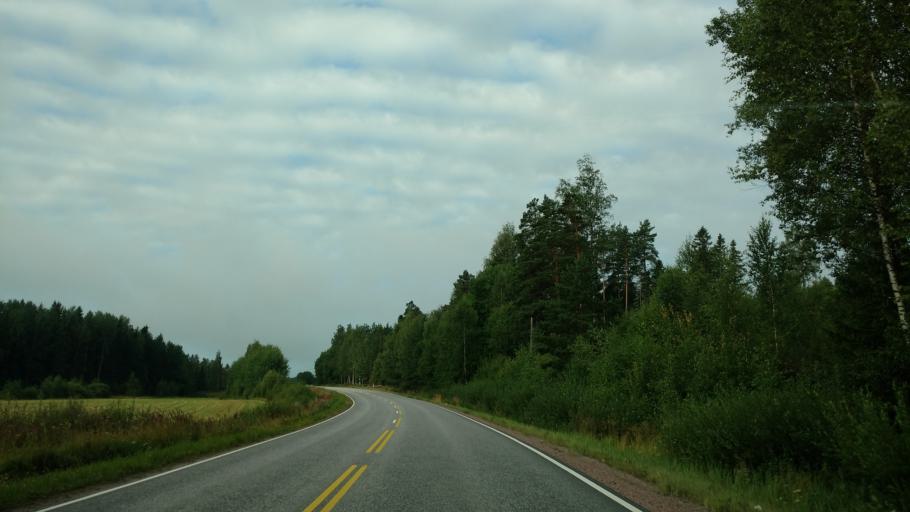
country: FI
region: Varsinais-Suomi
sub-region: Aboland-Turunmaa
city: Kimito
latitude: 60.1496
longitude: 22.6961
